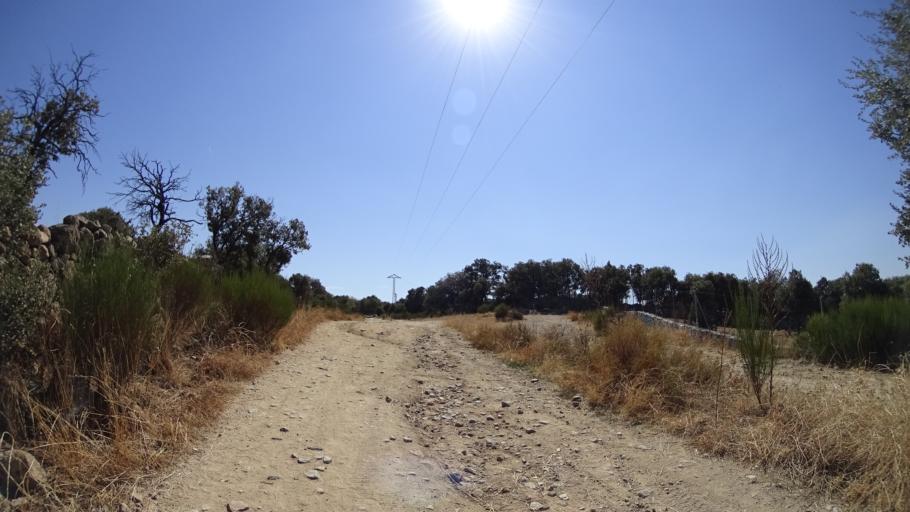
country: ES
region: Madrid
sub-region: Provincia de Madrid
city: Collado-Villalba
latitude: 40.6094
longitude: -4.0115
